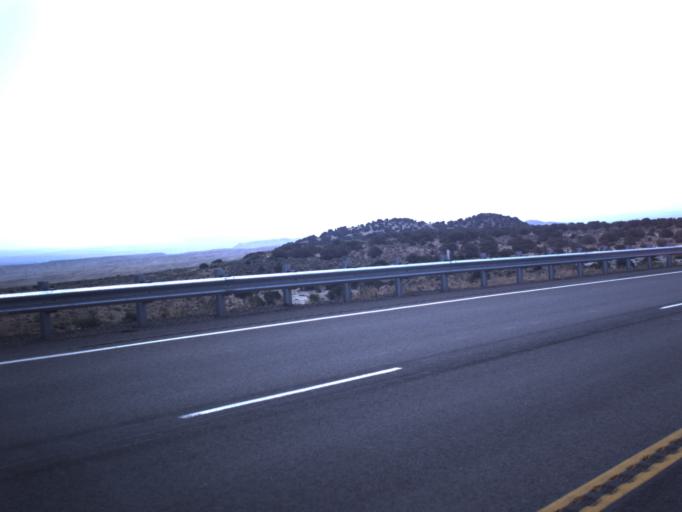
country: US
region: Utah
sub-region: Uintah County
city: Naples
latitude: 40.3434
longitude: -109.4845
